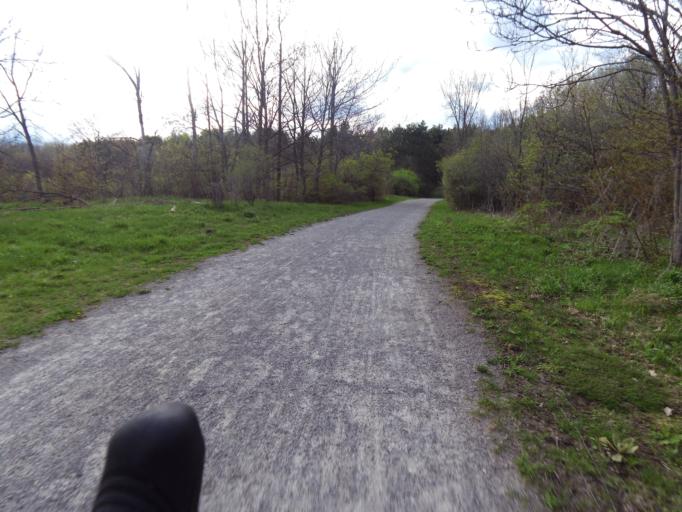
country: CA
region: Ontario
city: Ottawa
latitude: 45.3166
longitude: -75.7165
